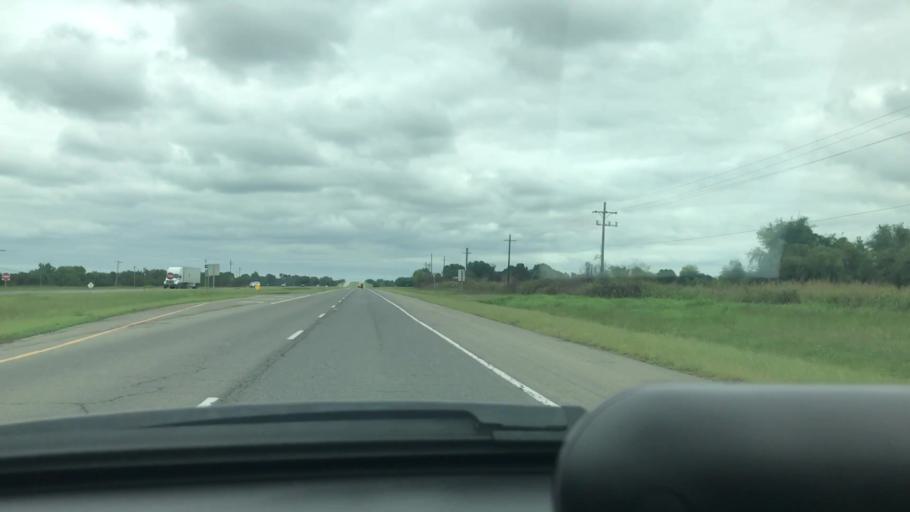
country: US
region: Oklahoma
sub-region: Wagoner County
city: Wagoner
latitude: 35.8632
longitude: -95.4026
